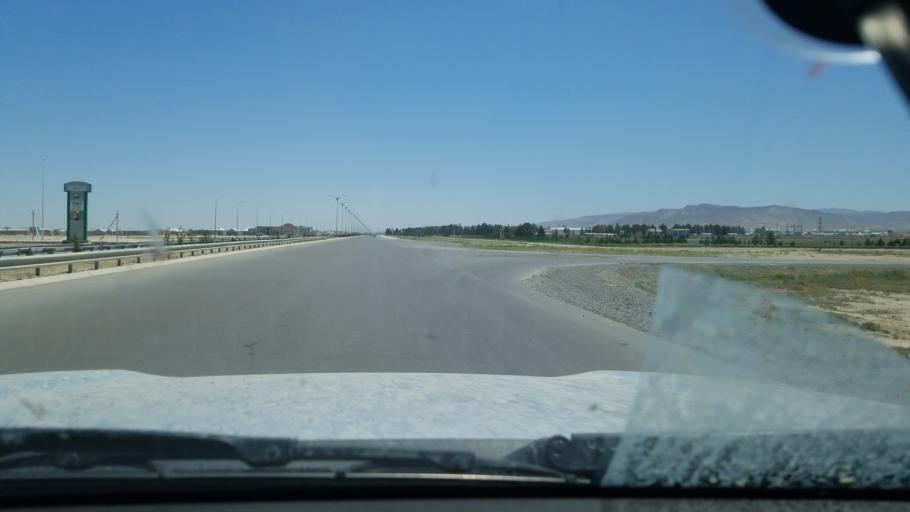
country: TM
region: Balkan
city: Serdar
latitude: 39.0051
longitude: 56.2518
